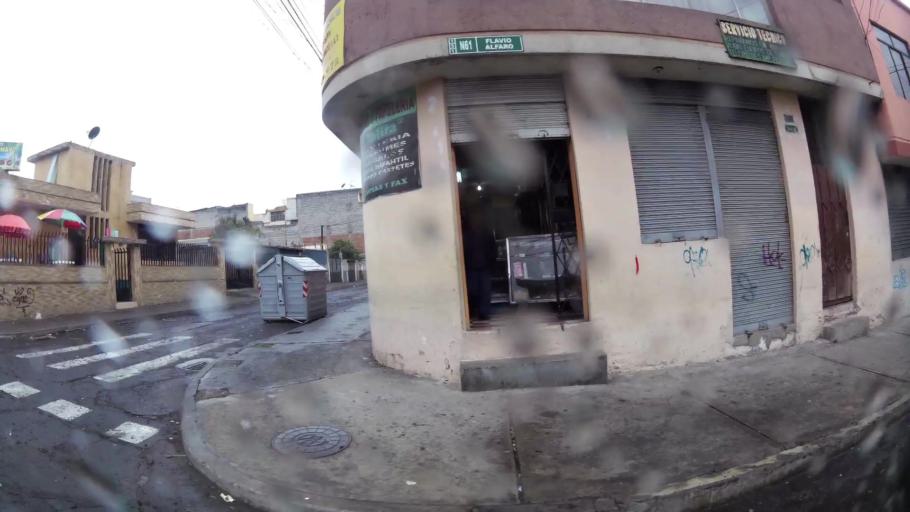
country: EC
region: Pichincha
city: Quito
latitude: -0.1236
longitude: -78.4949
